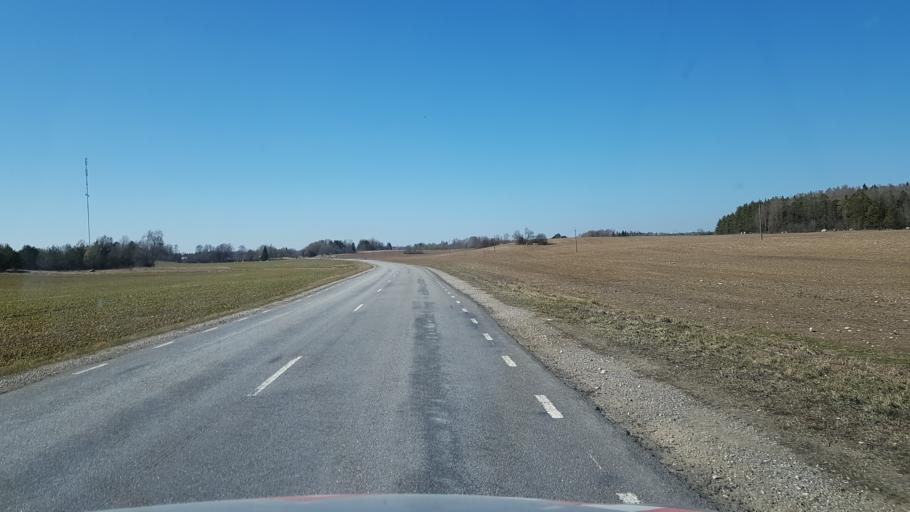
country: EE
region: Laeaene-Virumaa
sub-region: Tamsalu vald
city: Tamsalu
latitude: 59.1655
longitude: 26.1770
